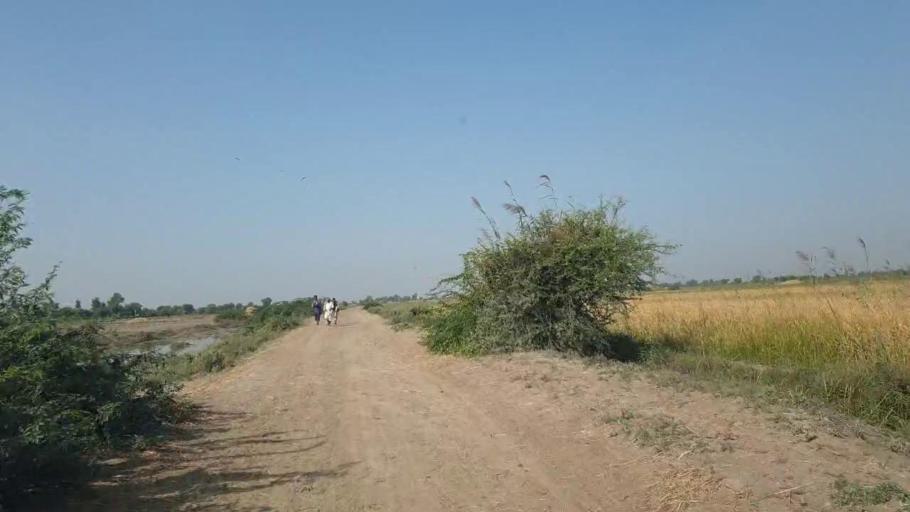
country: PK
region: Sindh
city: Badin
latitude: 24.5231
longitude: 68.7573
